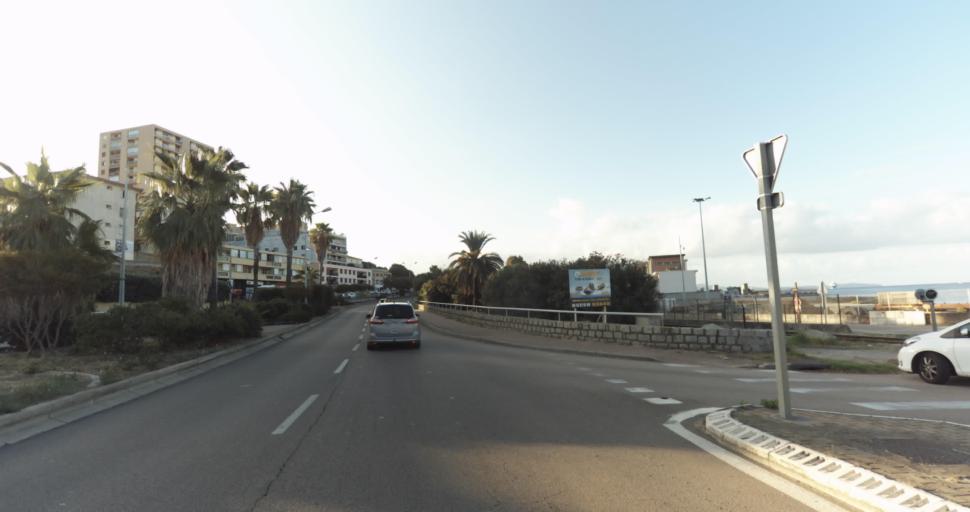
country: FR
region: Corsica
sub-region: Departement de la Corse-du-Sud
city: Ajaccio
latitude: 41.9319
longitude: 8.7563
